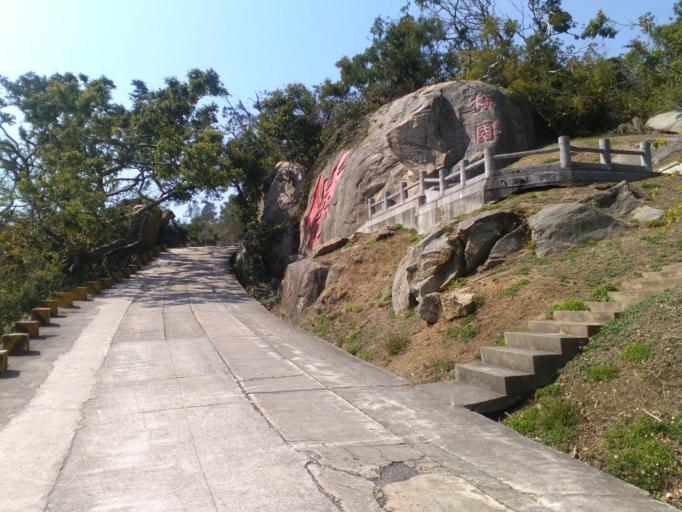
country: TW
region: Fukien
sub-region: Kinmen
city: Jincheng
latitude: 24.4635
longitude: 118.4170
